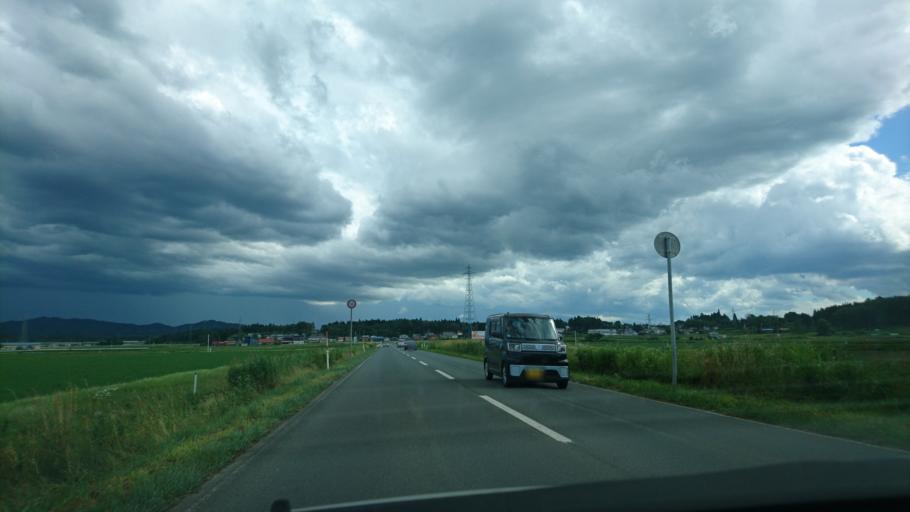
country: JP
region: Iwate
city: Kitakami
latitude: 39.3189
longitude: 141.1271
